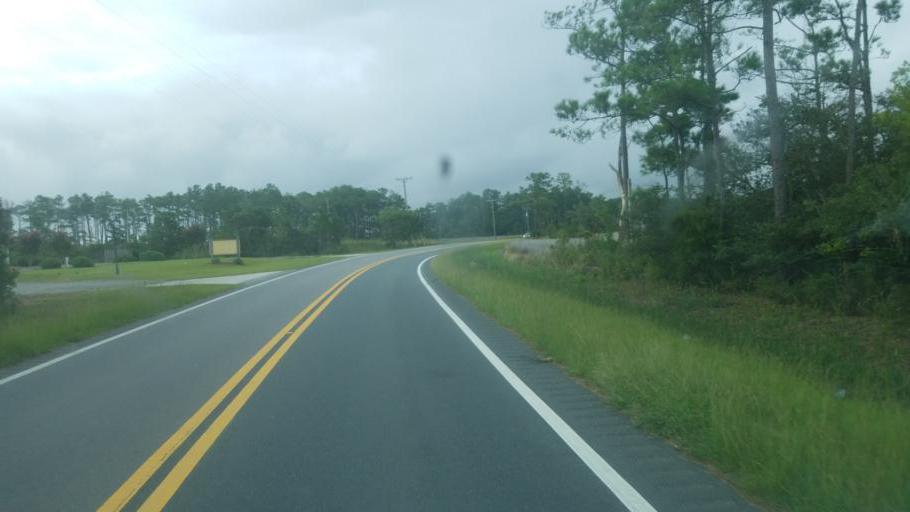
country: US
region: North Carolina
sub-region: Dare County
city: Wanchese
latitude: 35.8692
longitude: -75.6509
